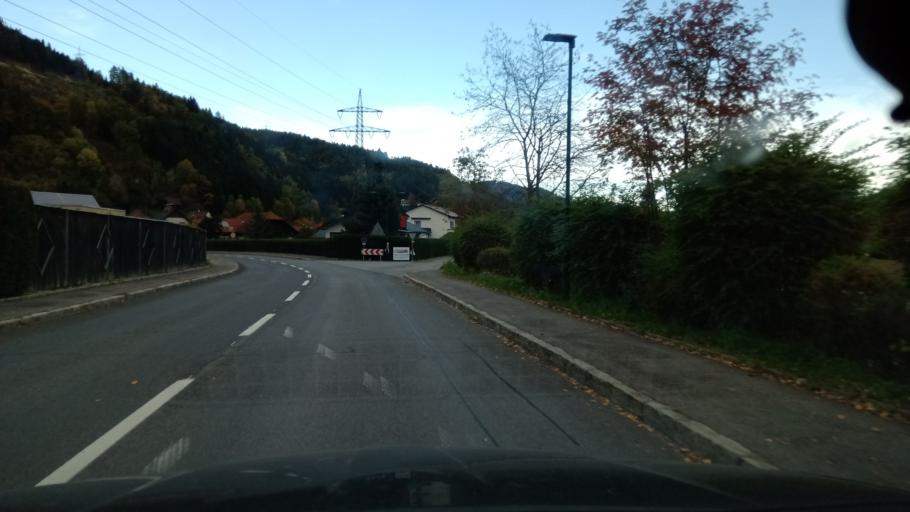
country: AT
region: Styria
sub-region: Politischer Bezirk Leoben
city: Proleb
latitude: 47.3981
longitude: 15.1410
